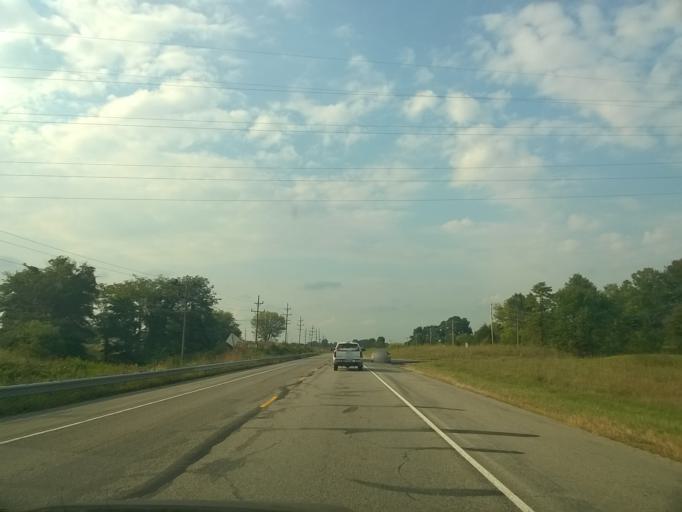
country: US
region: Indiana
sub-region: Putnam County
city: Cloverdale
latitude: 39.5561
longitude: -86.8117
